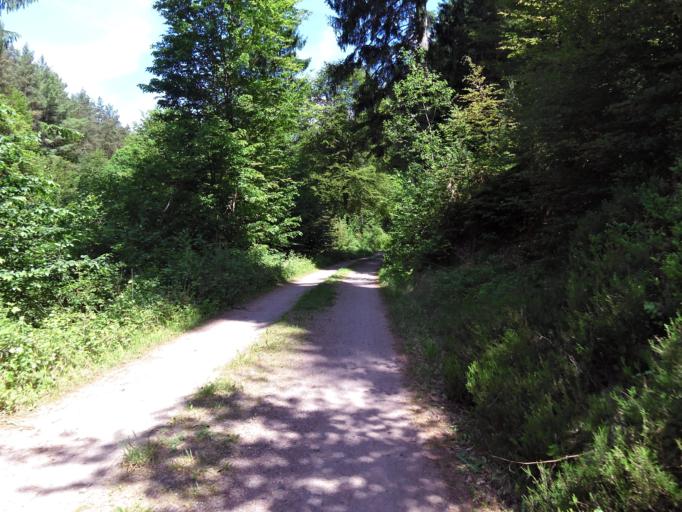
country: DE
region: Rheinland-Pfalz
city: Waldleiningen
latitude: 49.4053
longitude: 7.9033
